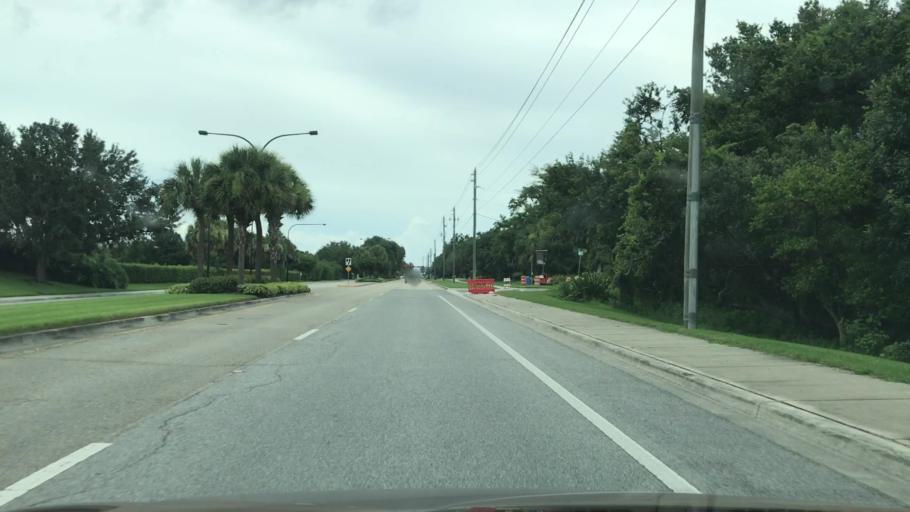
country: US
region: Florida
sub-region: Sarasota County
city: Bee Ridge
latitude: 27.2611
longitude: -82.4647
